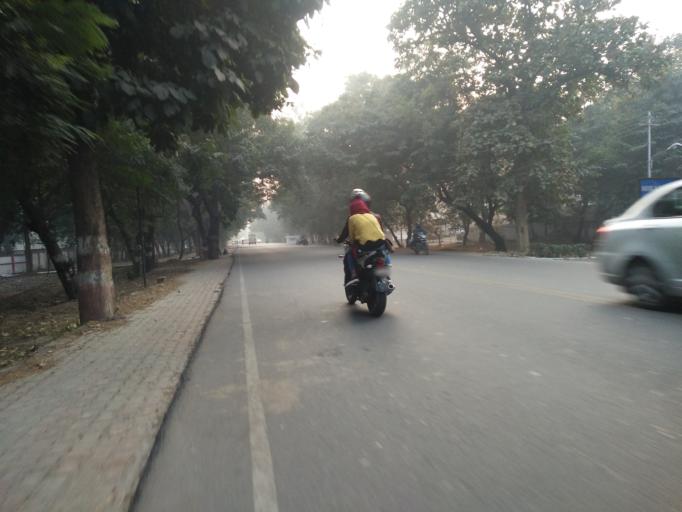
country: IN
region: Uttar Pradesh
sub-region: Lucknow District
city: Lucknow
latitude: 26.8113
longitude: 80.9423
